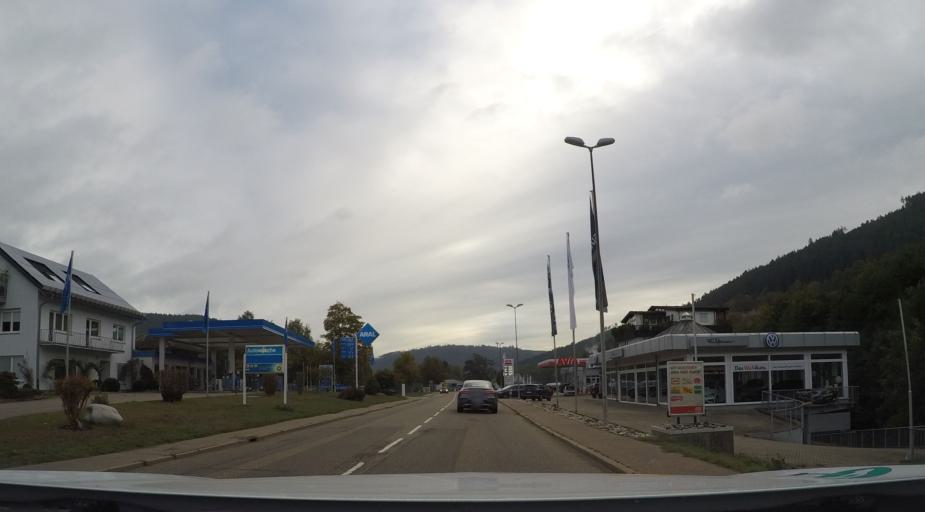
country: DE
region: Baden-Wuerttemberg
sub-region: Karlsruhe Region
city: Baiersbronn
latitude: 48.5122
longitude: 8.3769
